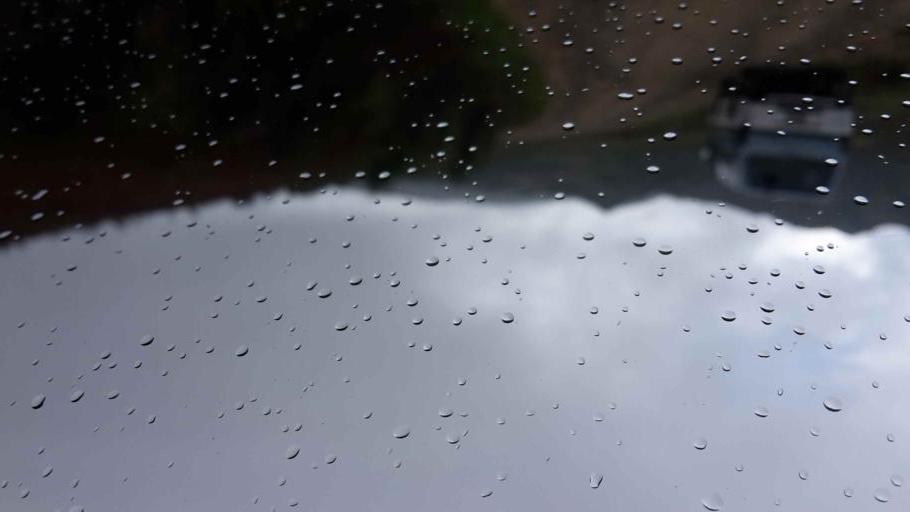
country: BO
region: Cochabamba
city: Cochabamba
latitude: -17.1501
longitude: -66.1049
